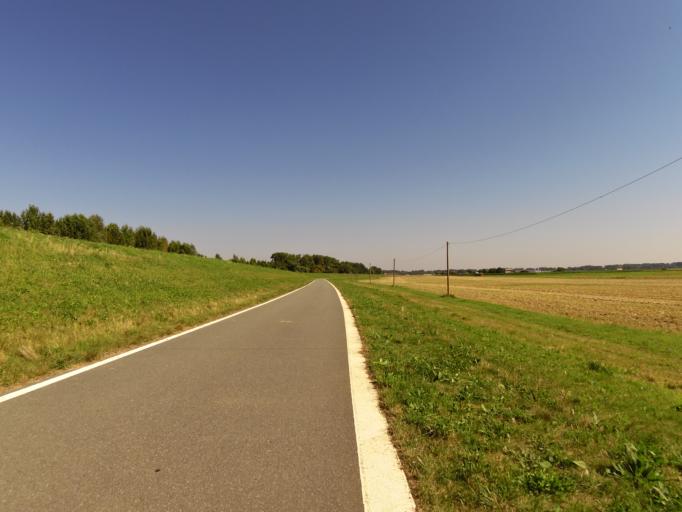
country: DE
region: Rheinland-Pfalz
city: Nackenheim
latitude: 49.9015
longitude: 8.3588
